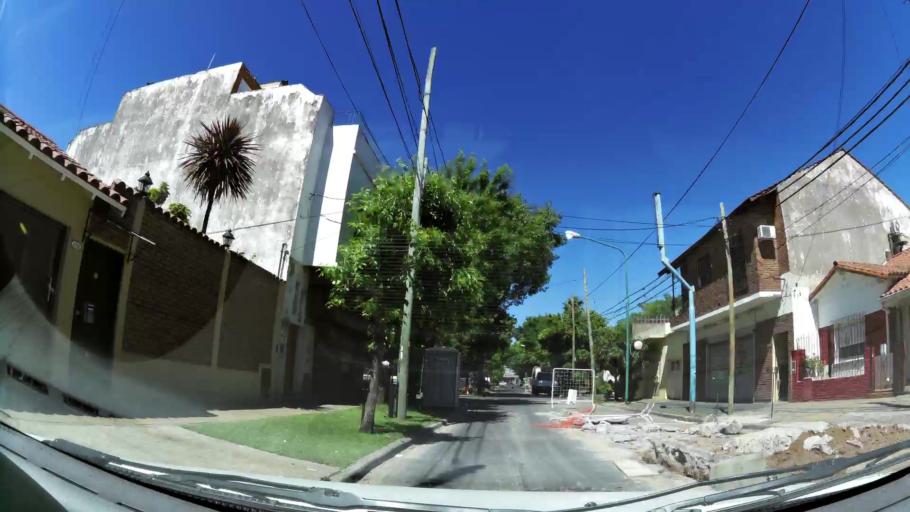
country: AR
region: Buenos Aires
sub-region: Partido de General San Martin
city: General San Martin
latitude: -34.5380
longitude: -58.5422
